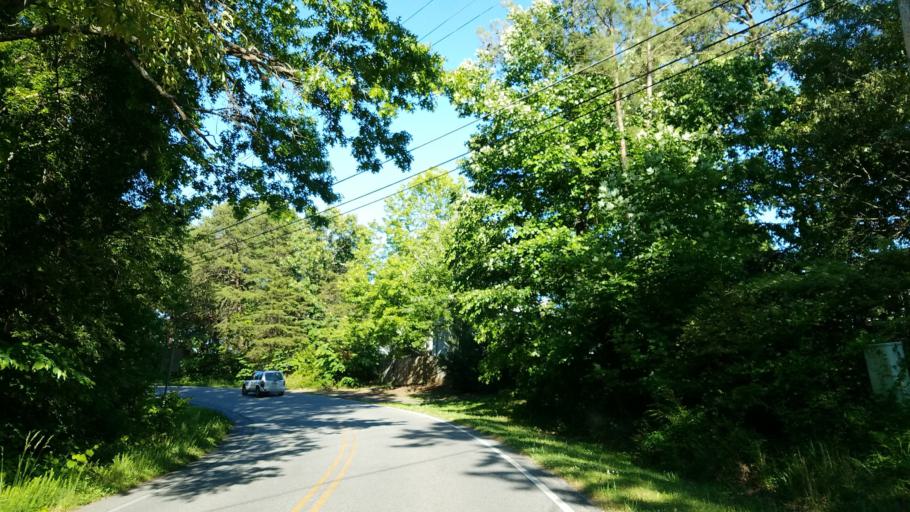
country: US
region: Georgia
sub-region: Cherokee County
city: Holly Springs
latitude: 34.1738
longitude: -84.5445
